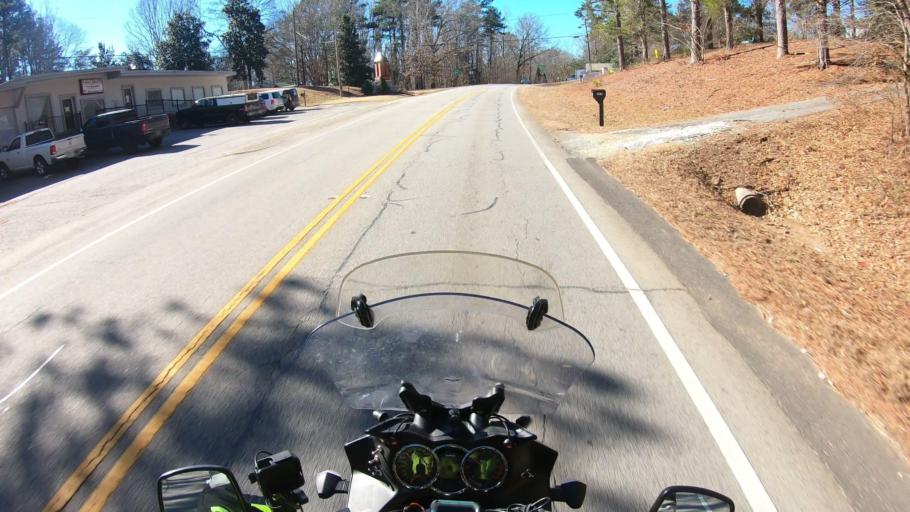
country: US
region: Georgia
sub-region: Paulding County
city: Dallas
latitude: 33.9129
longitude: -84.8591
